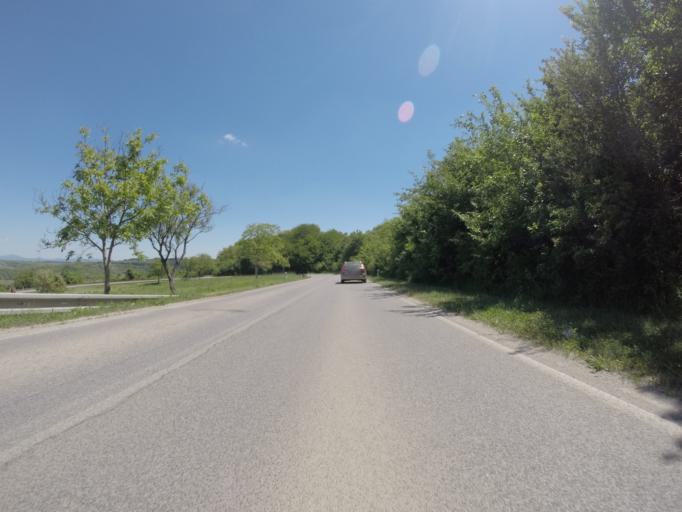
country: SK
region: Trnavsky
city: Hlohovec
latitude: 48.4142
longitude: 17.7946
